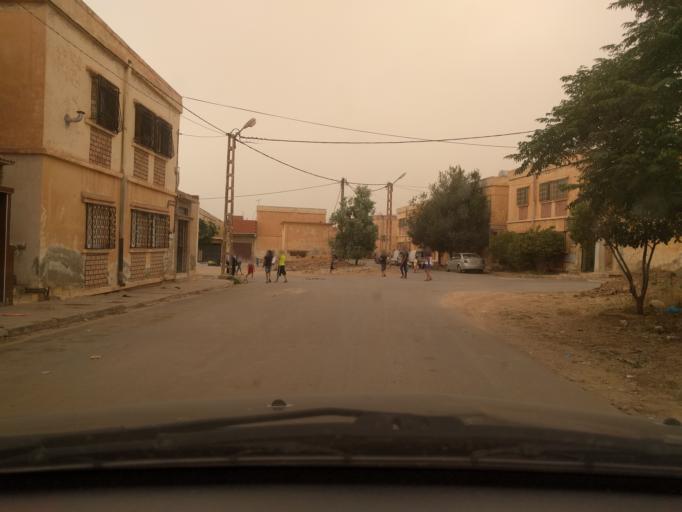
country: DZ
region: Tiaret
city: Frenda
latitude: 35.0680
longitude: 1.0625
